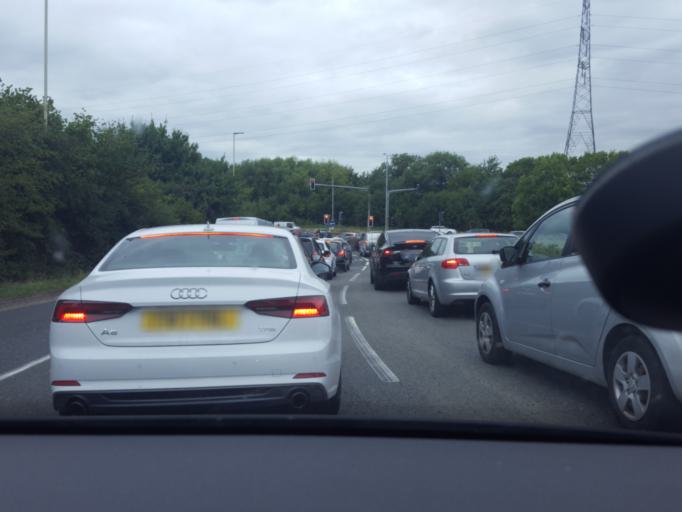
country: GB
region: England
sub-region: Leicestershire
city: Enderby
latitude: 52.5996
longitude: -1.1880
